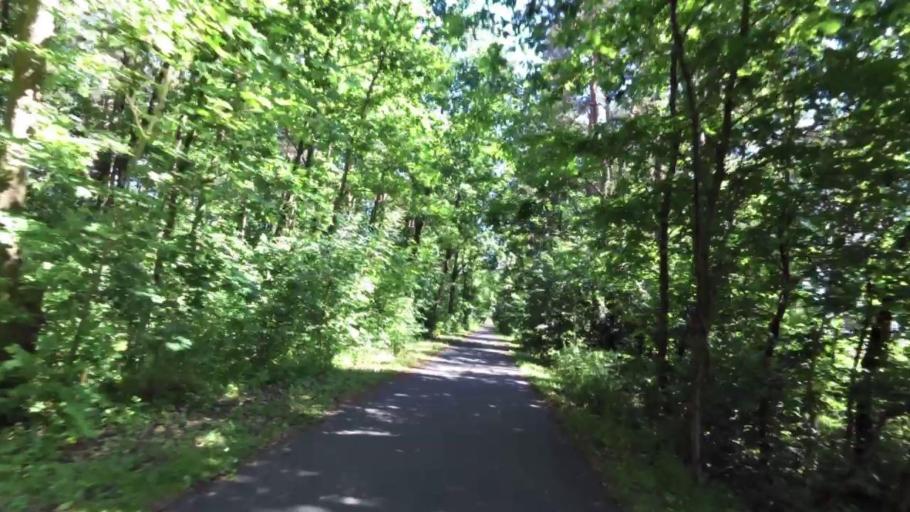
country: PL
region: West Pomeranian Voivodeship
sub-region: Powiat bialogardzki
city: Karlino
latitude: 54.0495
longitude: 15.8786
